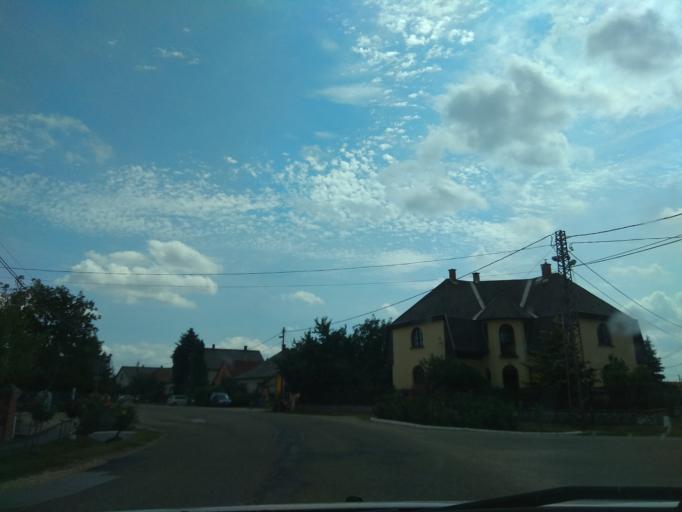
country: HU
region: Borsod-Abauj-Zemplen
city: Sajolad
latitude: 48.0354
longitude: 20.8883
